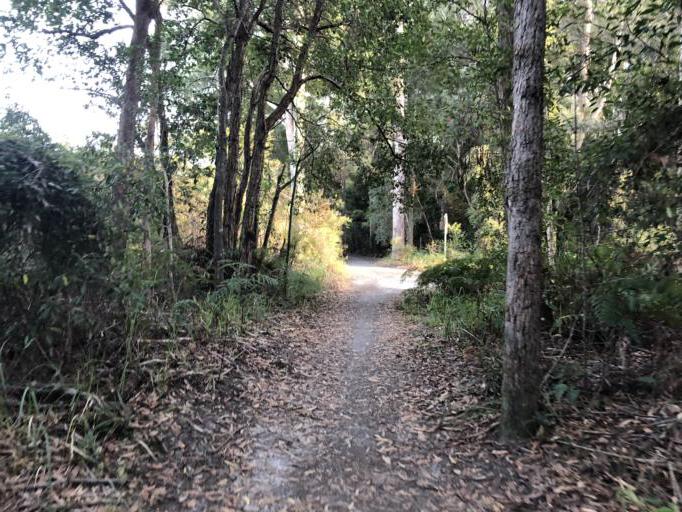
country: AU
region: New South Wales
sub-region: Coffs Harbour
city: Coffs Harbour
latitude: -30.3013
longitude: 153.1271
